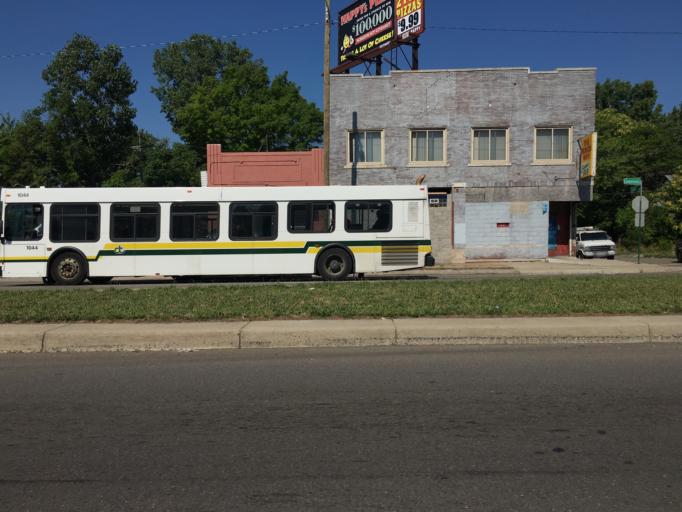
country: US
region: Michigan
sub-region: Wayne County
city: Highland Park
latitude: 42.4016
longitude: -83.1402
